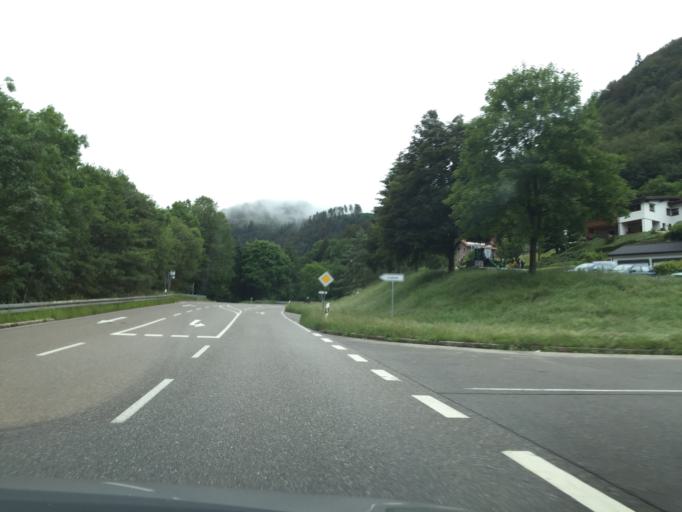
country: DE
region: Baden-Wuerttemberg
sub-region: Freiburg Region
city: Todtnau
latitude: 47.8330
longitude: 7.9386
